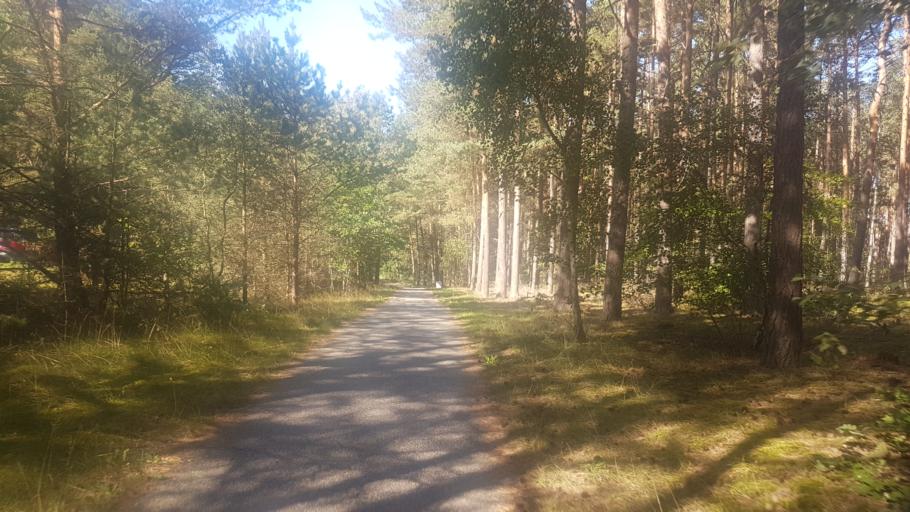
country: DE
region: Mecklenburg-Vorpommern
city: Glowe
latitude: 54.5773
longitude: 13.4149
